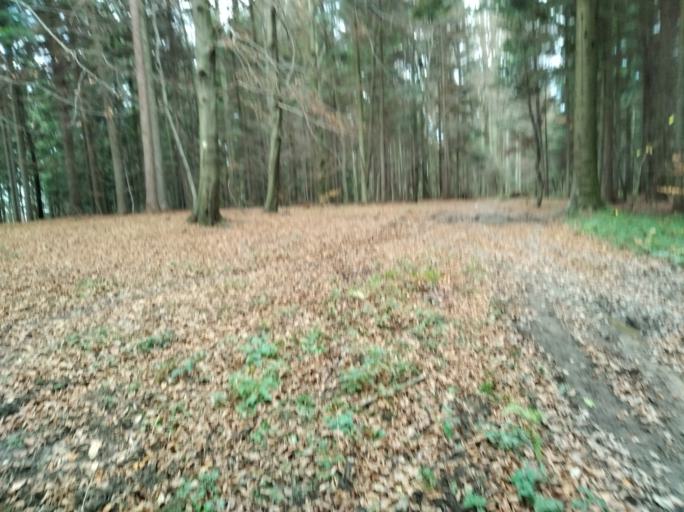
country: PL
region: Subcarpathian Voivodeship
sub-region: Powiat strzyzowski
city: Jawornik
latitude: 49.8632
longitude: 21.8553
